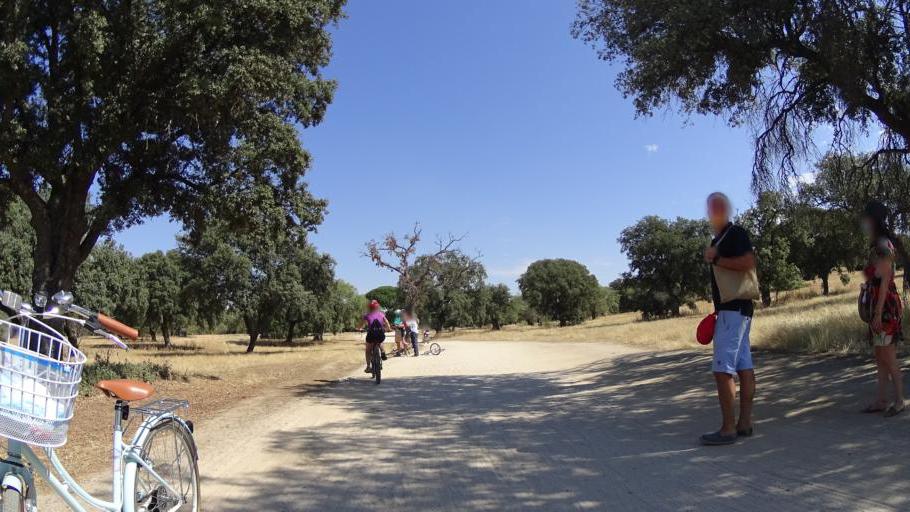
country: ES
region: Madrid
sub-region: Provincia de Madrid
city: Boadilla del Monte
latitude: 40.4117
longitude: -3.8655
